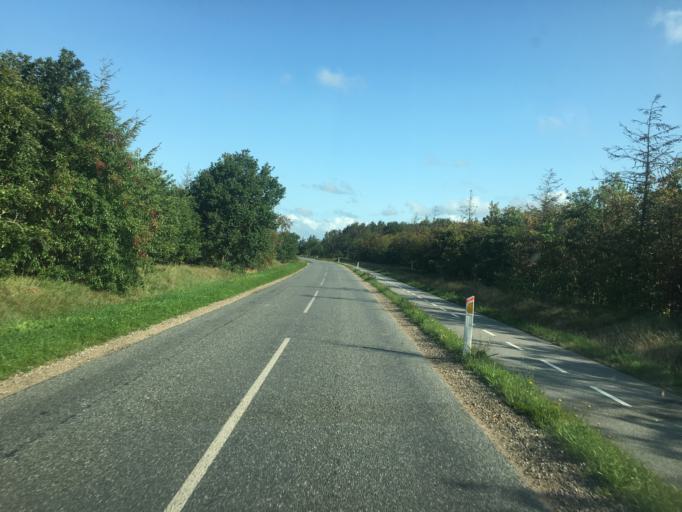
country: DK
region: South Denmark
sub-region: Tonder Kommune
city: Sherrebek
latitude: 55.1256
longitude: 8.7608
